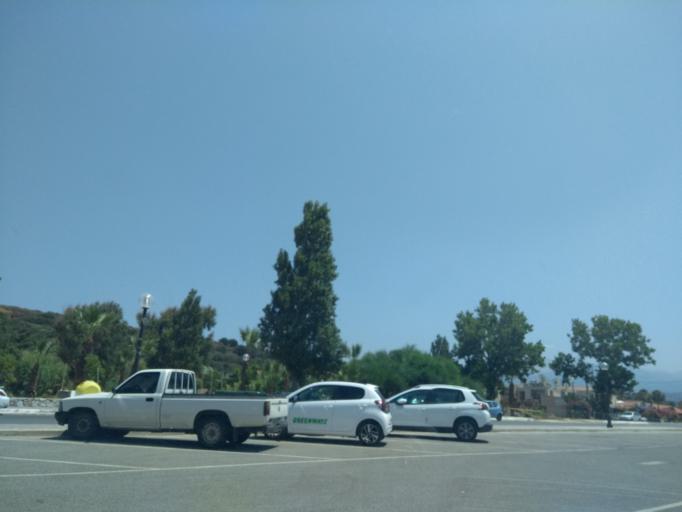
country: GR
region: Crete
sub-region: Nomos Chanias
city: Daratsos
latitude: 35.5113
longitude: 23.9894
